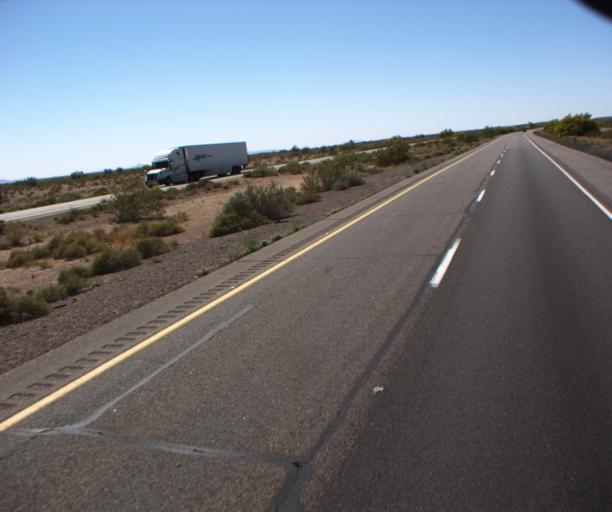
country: US
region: Arizona
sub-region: Maricopa County
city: Gila Bend
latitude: 32.8943
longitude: -113.0363
